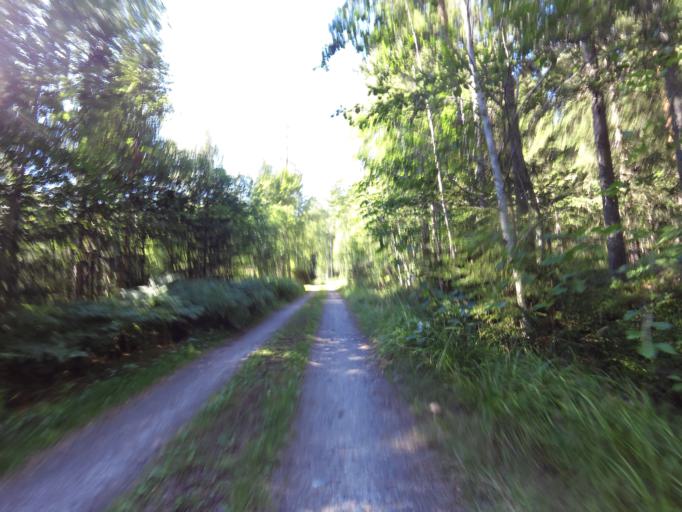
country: SE
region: Gaevleborg
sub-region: Hofors Kommun
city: Hofors
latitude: 60.5809
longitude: 16.4074
